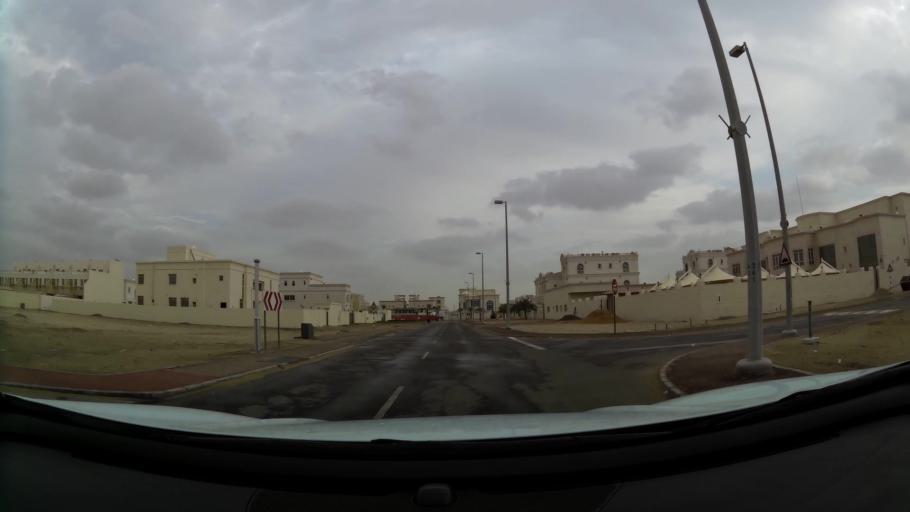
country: AE
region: Abu Dhabi
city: Abu Dhabi
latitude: 24.3471
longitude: 54.6231
